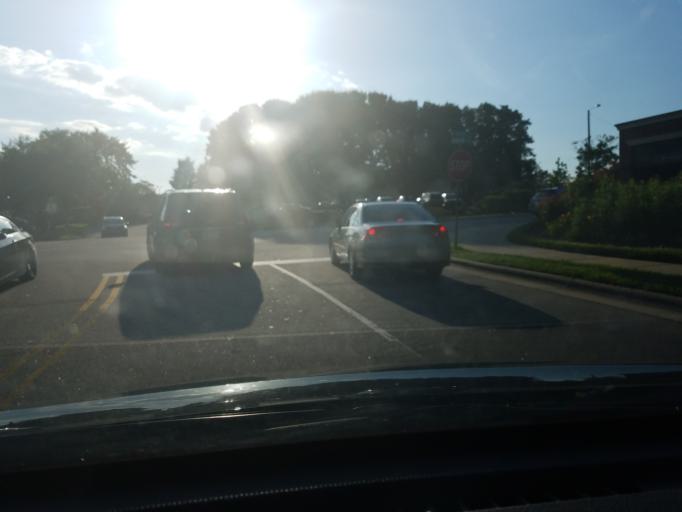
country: US
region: North Carolina
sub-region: Orange County
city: Chapel Hill
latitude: 35.9513
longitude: -78.9941
